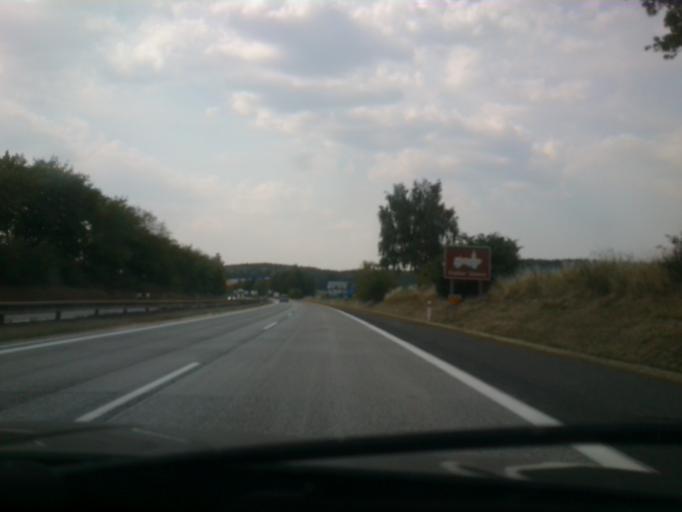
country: CZ
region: Central Bohemia
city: Divisov
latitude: 49.8308
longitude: 14.8610
